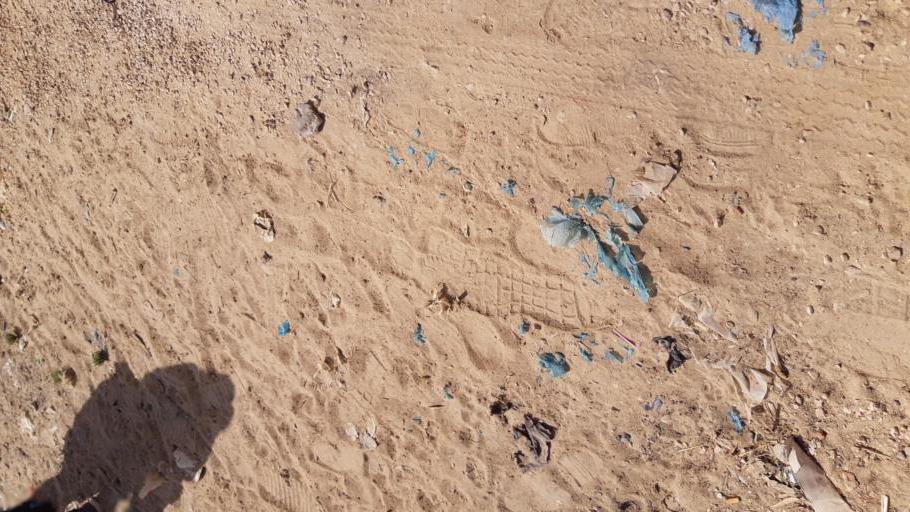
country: TN
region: Qabis
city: Gabes
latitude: 33.8675
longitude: 10.0807
